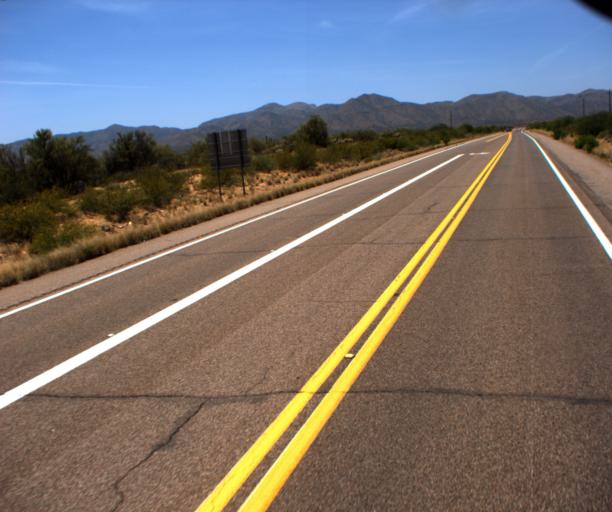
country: US
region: Arizona
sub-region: Gila County
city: Miami
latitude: 33.6150
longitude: -111.0314
